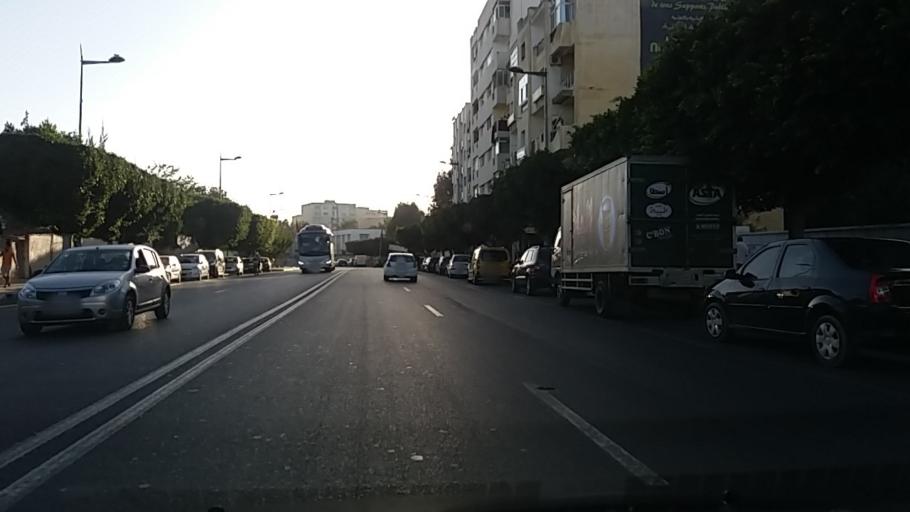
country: MA
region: Gharb-Chrarda-Beni Hssen
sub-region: Kenitra Province
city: Kenitra
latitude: 34.2630
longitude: -6.5748
